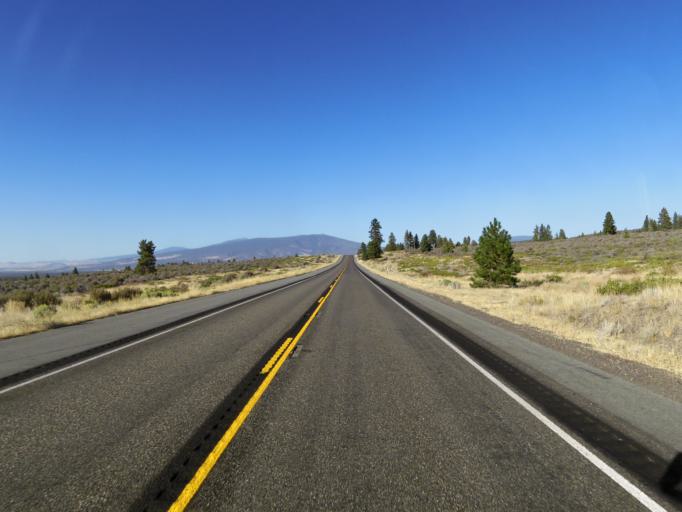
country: US
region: California
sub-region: Siskiyou County
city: Weed
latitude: 41.4879
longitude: -122.3380
